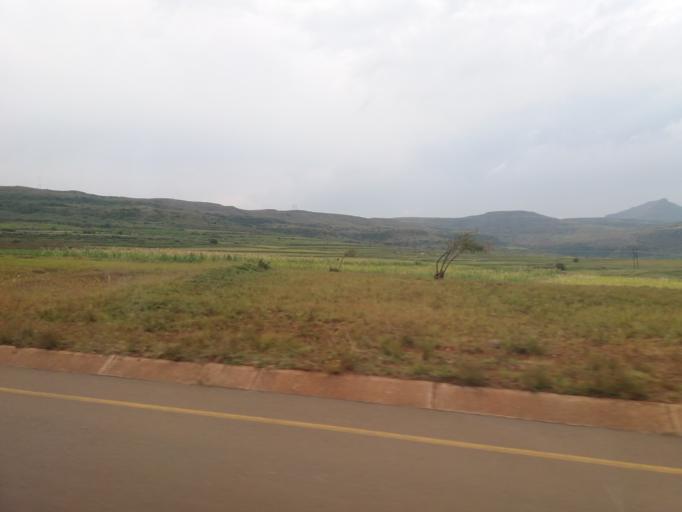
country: LS
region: Berea
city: Teyateyaneng
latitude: -29.3246
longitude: 27.7655
